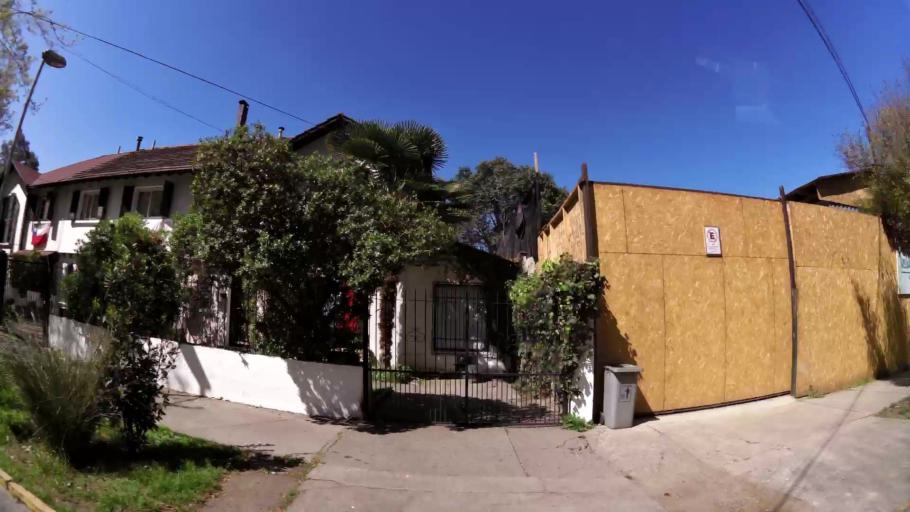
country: CL
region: Santiago Metropolitan
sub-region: Provincia de Santiago
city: Villa Presidente Frei, Nunoa, Santiago, Chile
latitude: -33.4131
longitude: -70.5758
